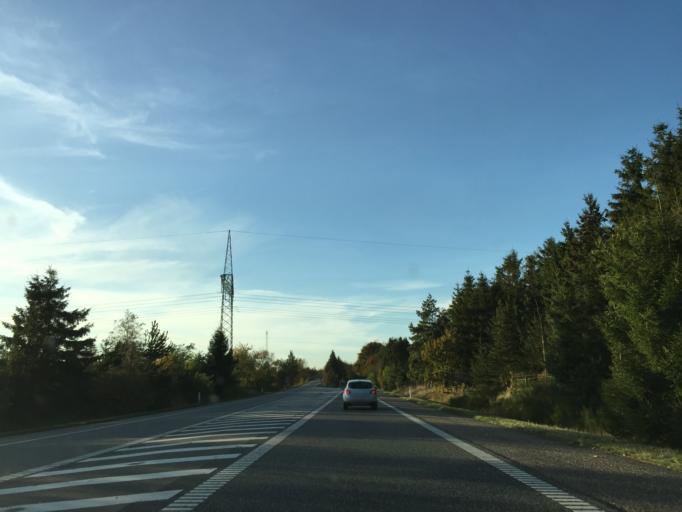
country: DK
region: South Denmark
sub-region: Aabenraa Kommune
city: Krusa
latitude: 54.8730
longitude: 9.3850
